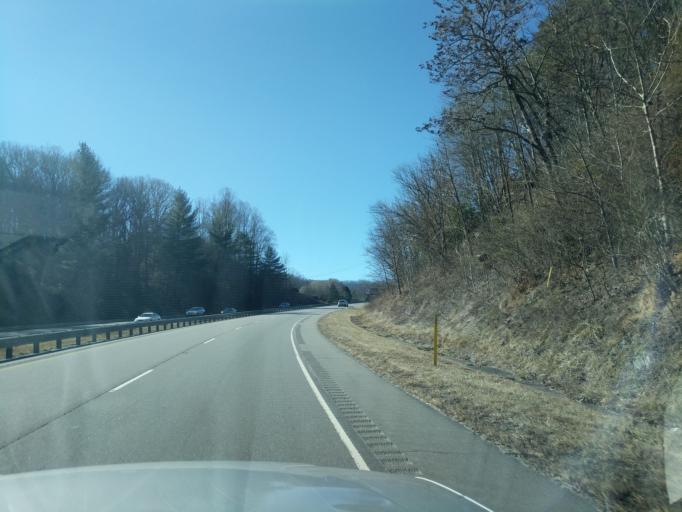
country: US
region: North Carolina
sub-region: Jackson County
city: Cullowhee
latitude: 35.3949
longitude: -83.1378
